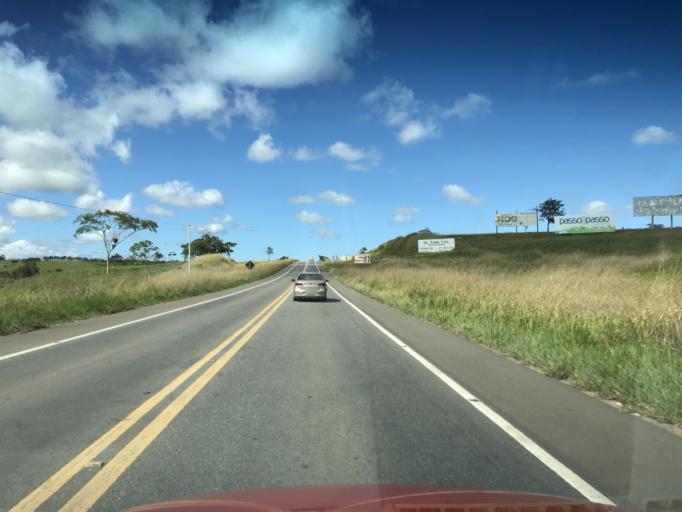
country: BR
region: Bahia
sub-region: Conceicao Do Almeida
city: Muritiba
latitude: -12.9348
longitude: -39.2529
